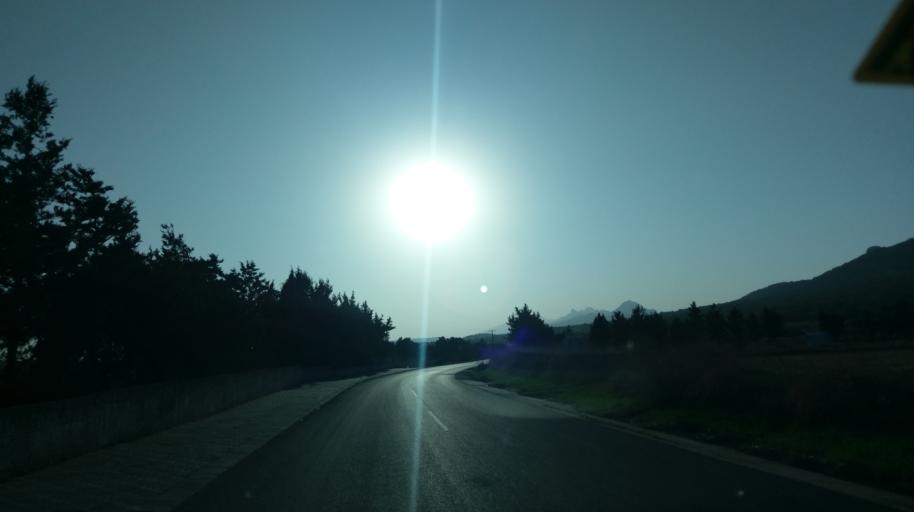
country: CY
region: Ammochostos
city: Leonarisso
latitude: 35.4400
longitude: 34.0267
